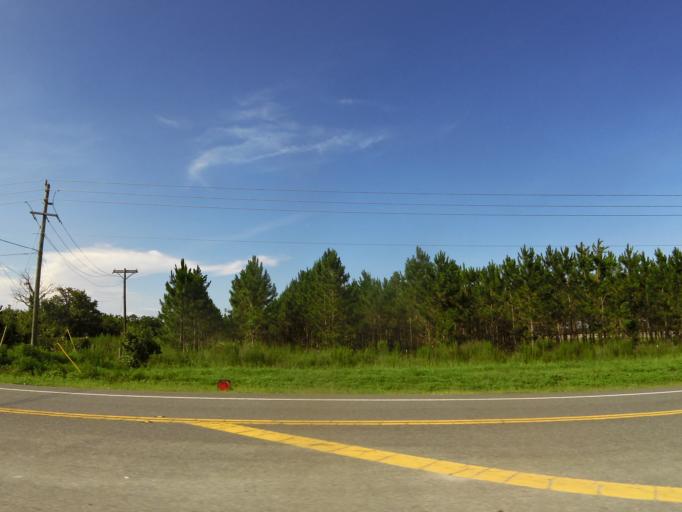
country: US
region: Florida
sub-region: Clay County
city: Green Cove Springs
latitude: 29.9766
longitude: -81.5131
